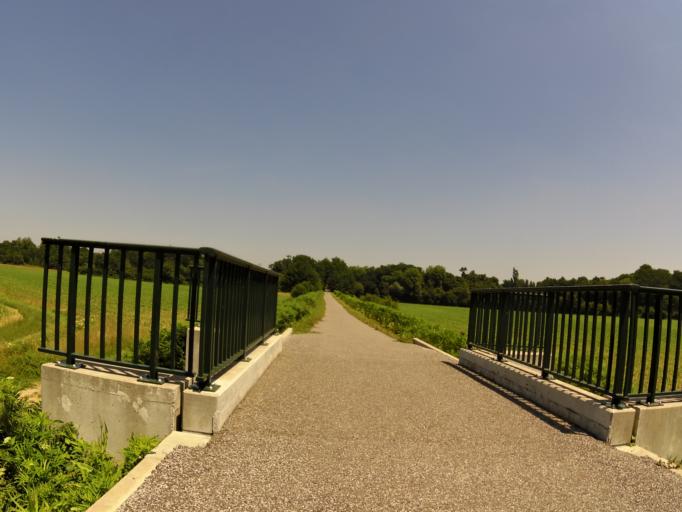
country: FR
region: Aquitaine
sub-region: Departement des Pyrenees-Atlantiques
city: Salies-de-Bearn
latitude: 43.4601
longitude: -0.9832
